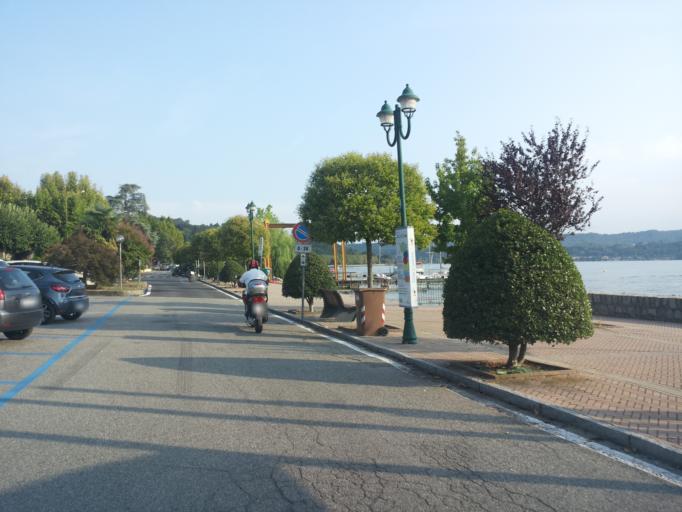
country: IT
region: Piedmont
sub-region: Provincia di Biella
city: Viverone
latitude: 45.4221
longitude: 8.0457
